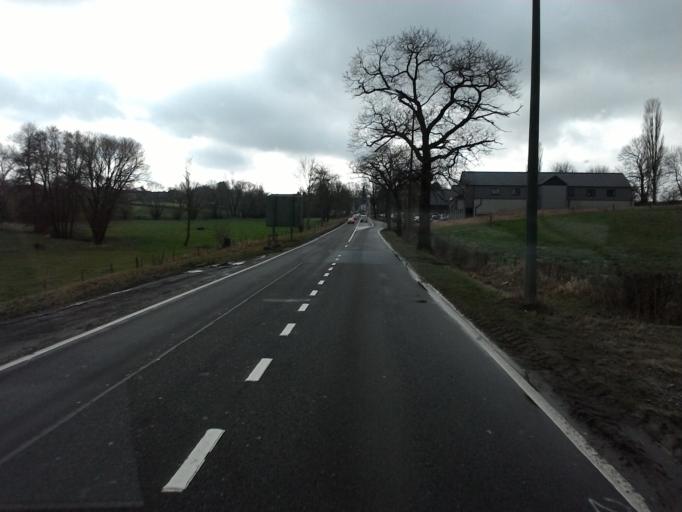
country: BE
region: Wallonia
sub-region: Province de Liege
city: Raeren
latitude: 50.6986
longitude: 6.0845
